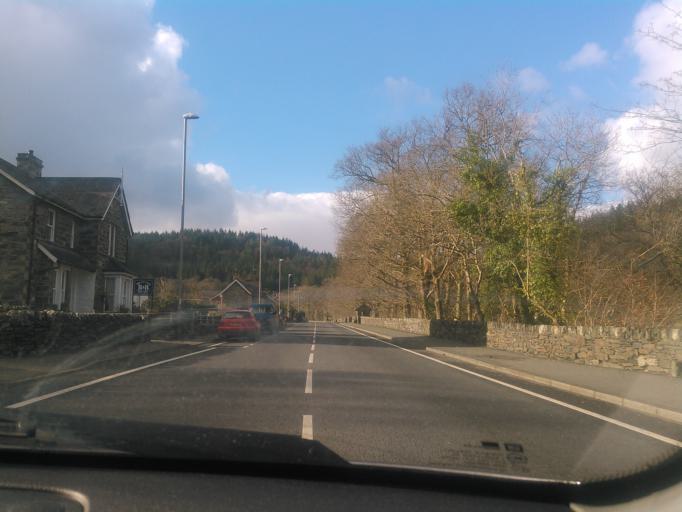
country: GB
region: Wales
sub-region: Conwy
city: Betws-y-Coed
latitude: 53.0929
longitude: -3.8162
